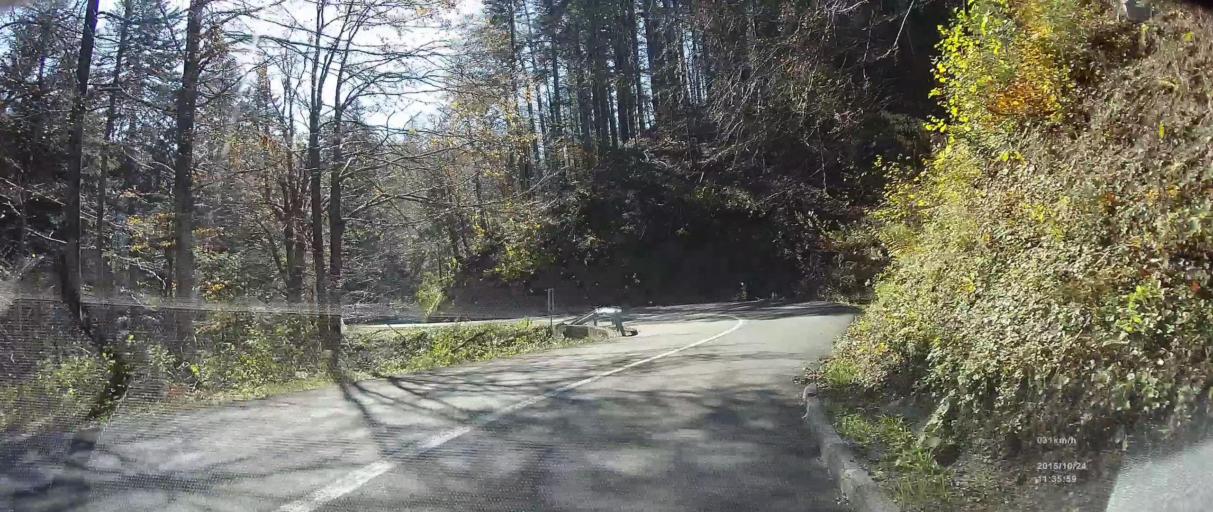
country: HR
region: Primorsko-Goranska
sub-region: Grad Delnice
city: Delnice
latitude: 45.3974
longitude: 14.7006
